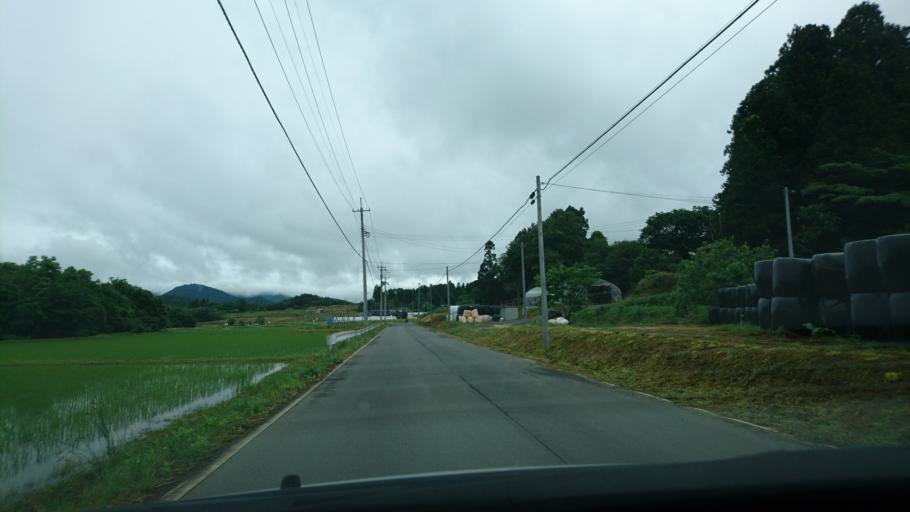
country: JP
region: Iwate
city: Ichinoseki
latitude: 38.9206
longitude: 141.2089
